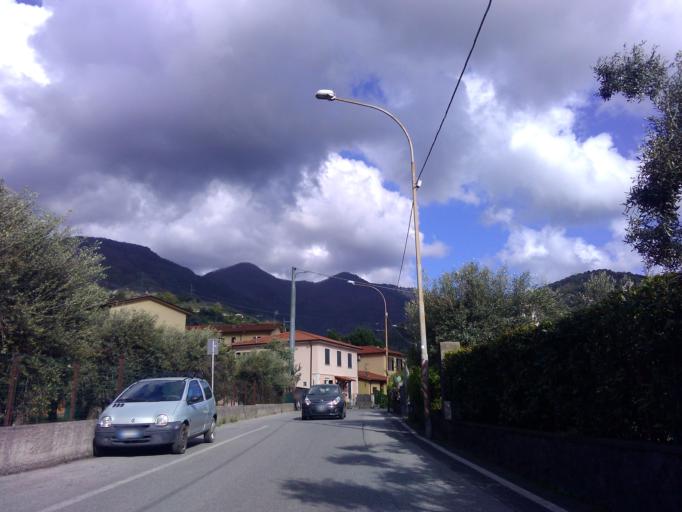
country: IT
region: Tuscany
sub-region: Provincia di Lucca
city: Seravezza
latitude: 43.9823
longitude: 10.2184
